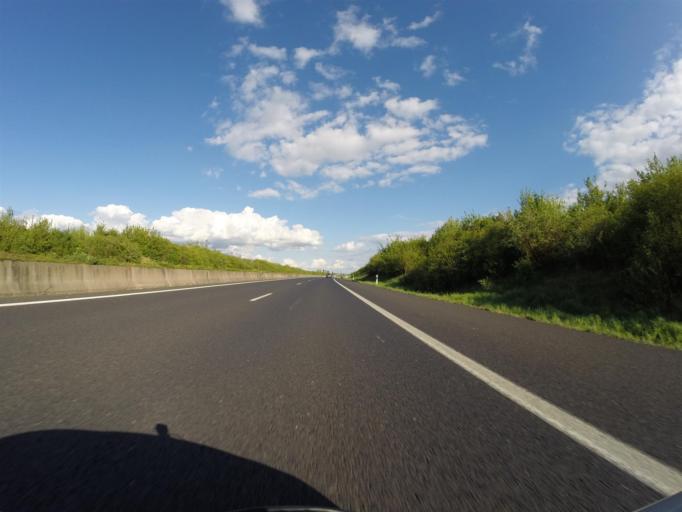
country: LU
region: Grevenmacher
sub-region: Canton de Remich
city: Mondorf-les-Bains
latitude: 49.4933
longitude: 6.3227
